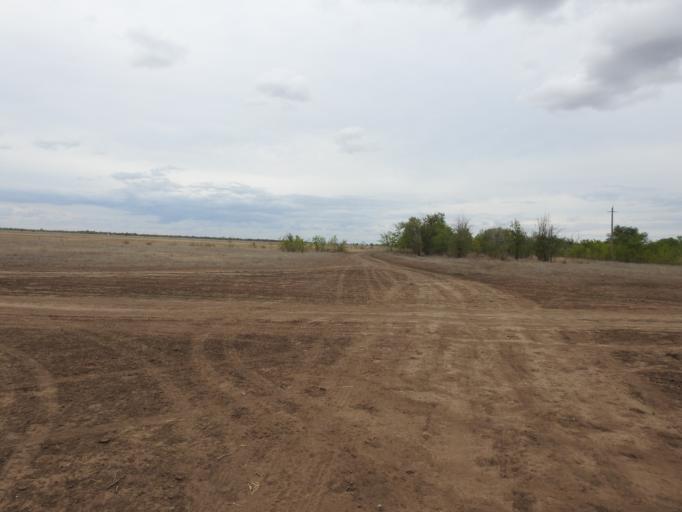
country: RU
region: Saratov
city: Rovnoye
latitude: 50.6437
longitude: 46.2060
